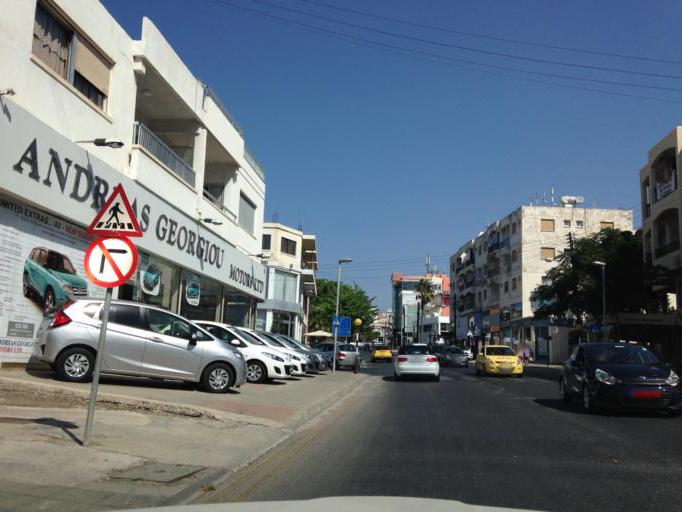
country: CY
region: Pafos
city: Paphos
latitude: 34.7703
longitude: 32.4176
